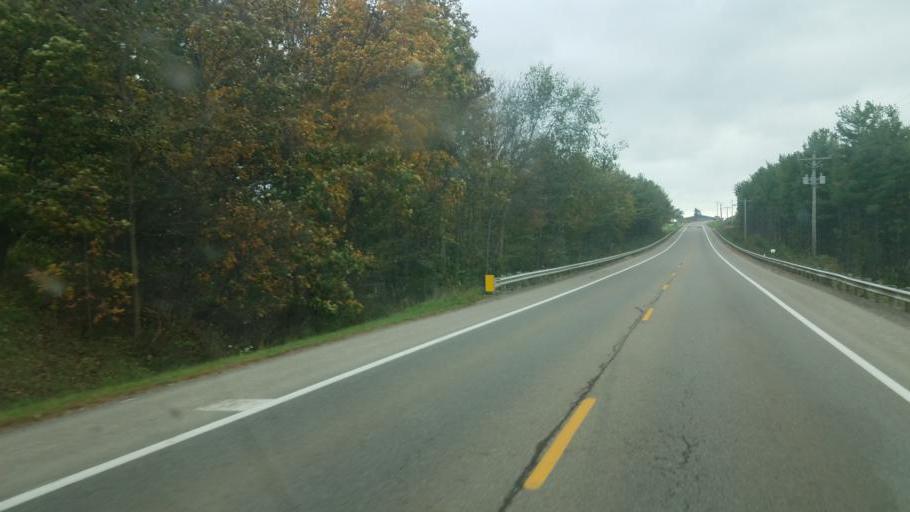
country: US
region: Ohio
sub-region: Tuscarawas County
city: Sugarcreek
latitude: 40.5179
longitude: -81.6969
